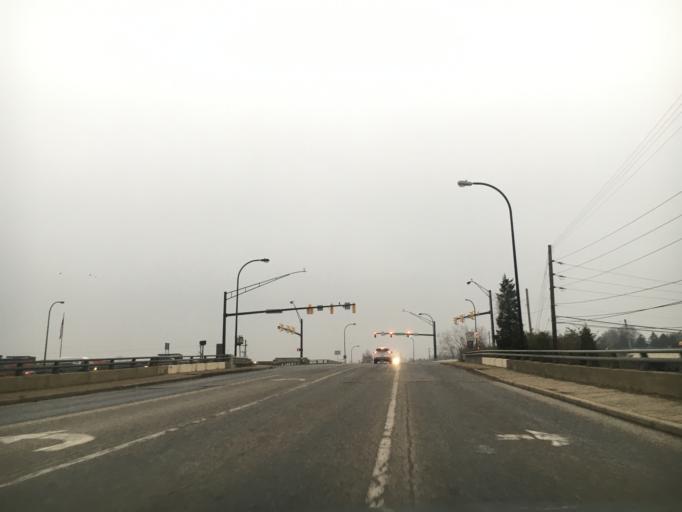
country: US
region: Ohio
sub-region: Summit County
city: Cuyahoga Falls
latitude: 41.1033
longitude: -81.4884
